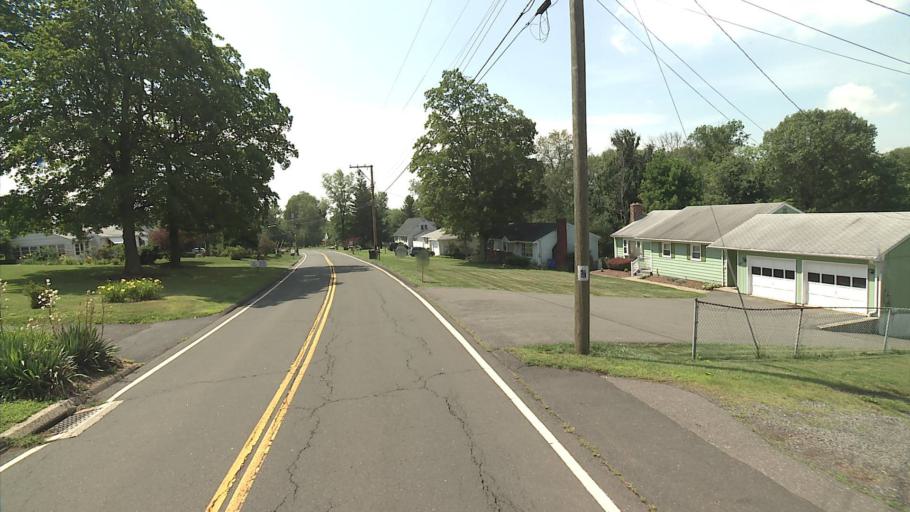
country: US
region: Connecticut
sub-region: Middlesex County
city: Middletown
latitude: 41.5554
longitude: -72.7027
